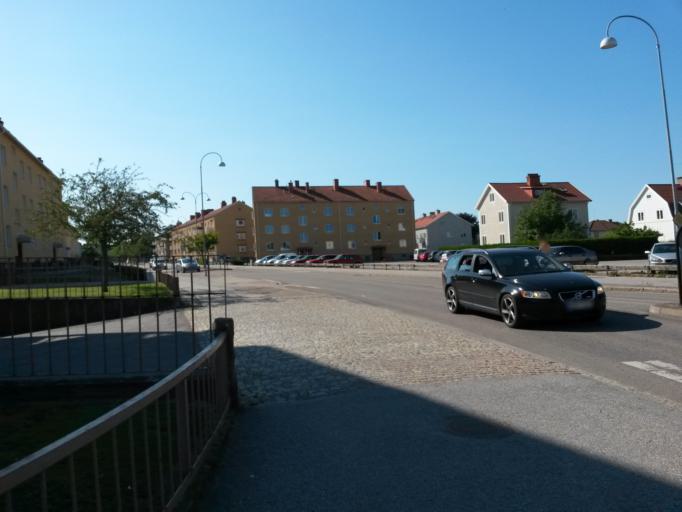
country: SE
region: Vaestra Goetaland
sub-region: Lidkopings Kommun
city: Lidkoping
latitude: 58.4987
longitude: 13.1712
